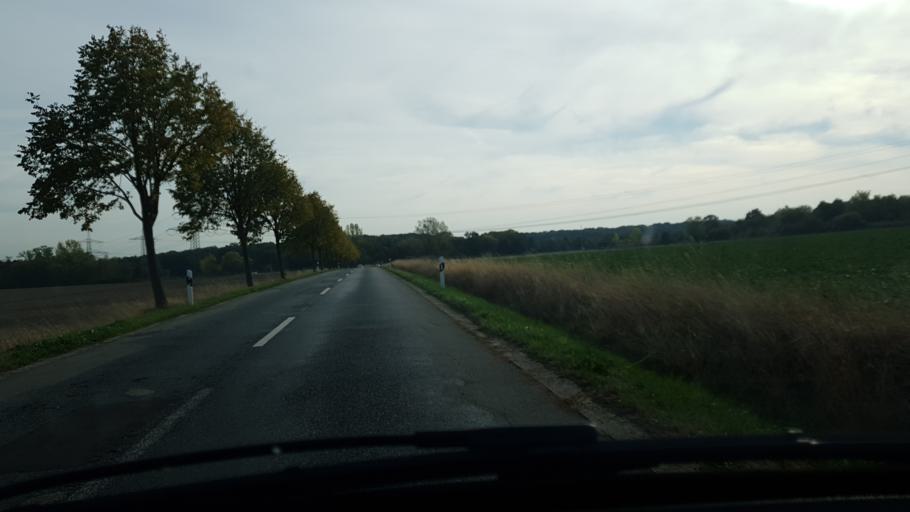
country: DE
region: Lower Saxony
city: Lehre
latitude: 52.3784
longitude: 10.6814
